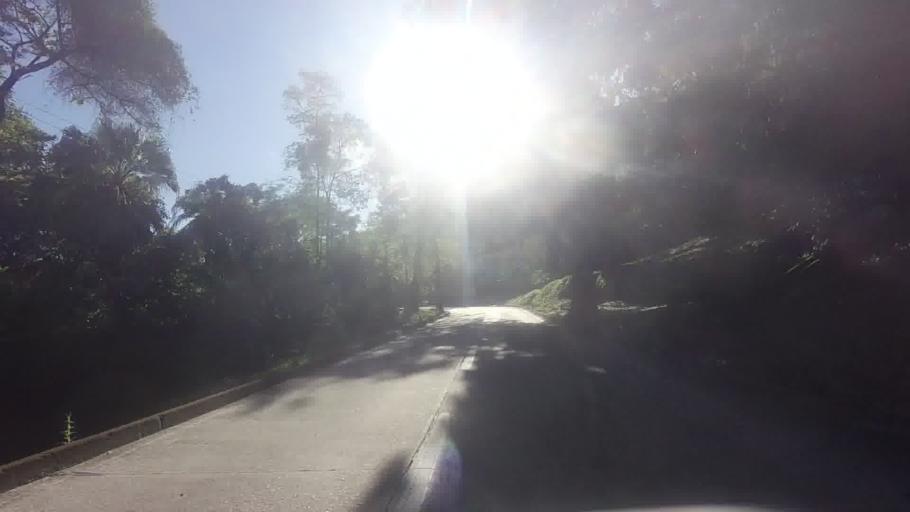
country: BR
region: Rio de Janeiro
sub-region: Petropolis
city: Petropolis
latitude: -22.5719
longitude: -43.2538
